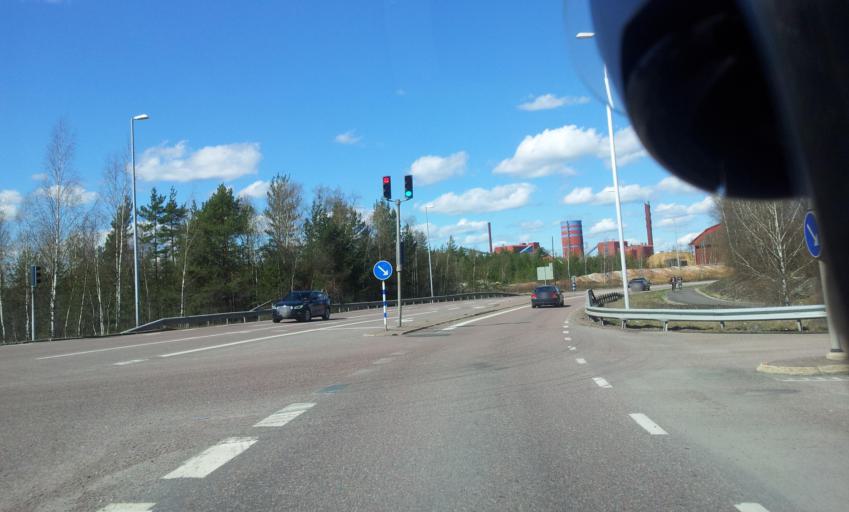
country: SE
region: Dalarna
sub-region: Faluns Kommun
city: Falun
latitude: 60.6028
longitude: 15.6173
